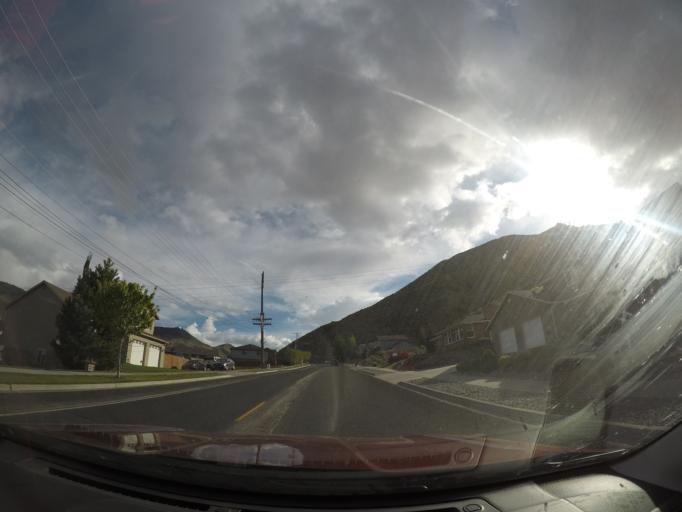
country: US
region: Washington
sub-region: Chelan County
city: South Wenatchee
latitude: 47.3907
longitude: -120.3094
